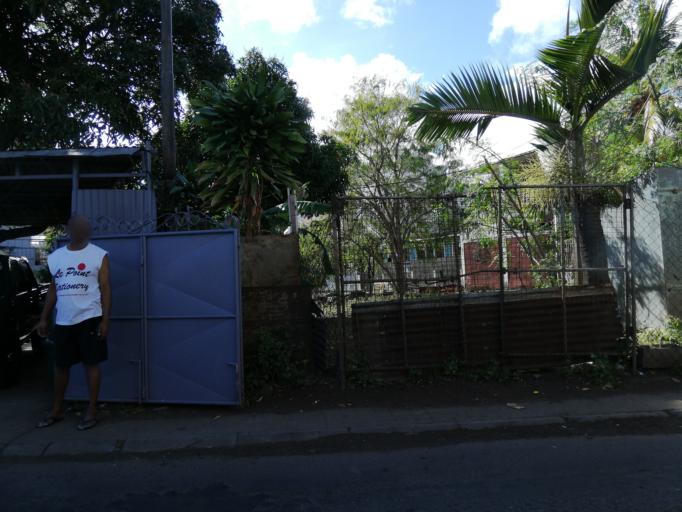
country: MU
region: Moka
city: Pailles
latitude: -20.1768
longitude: 57.4741
